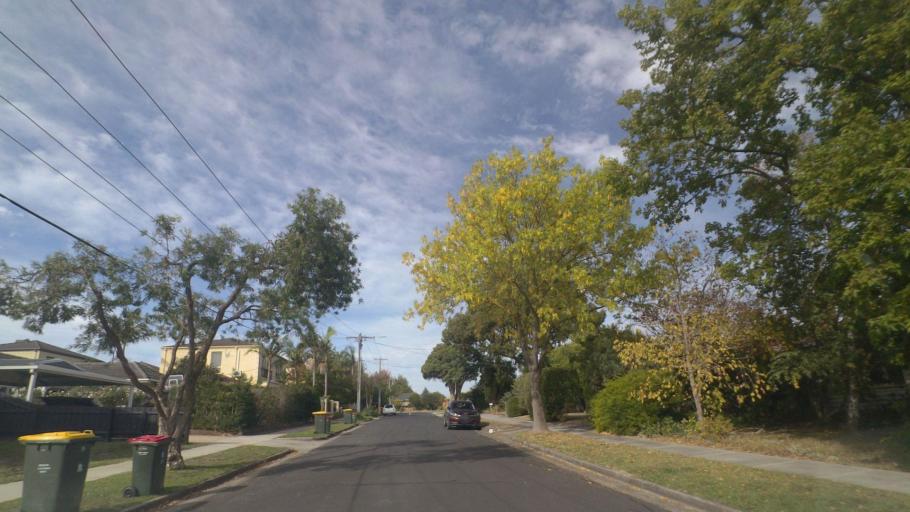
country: AU
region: Victoria
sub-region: Whitehorse
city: Blackburn South
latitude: -37.8347
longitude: 145.1407
